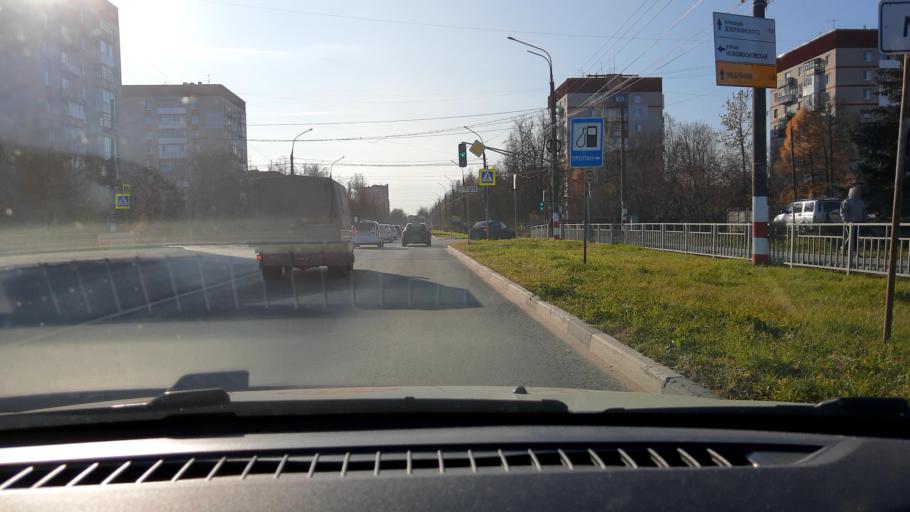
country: RU
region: Nizjnij Novgorod
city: Dzerzhinsk
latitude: 56.2559
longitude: 43.4669
